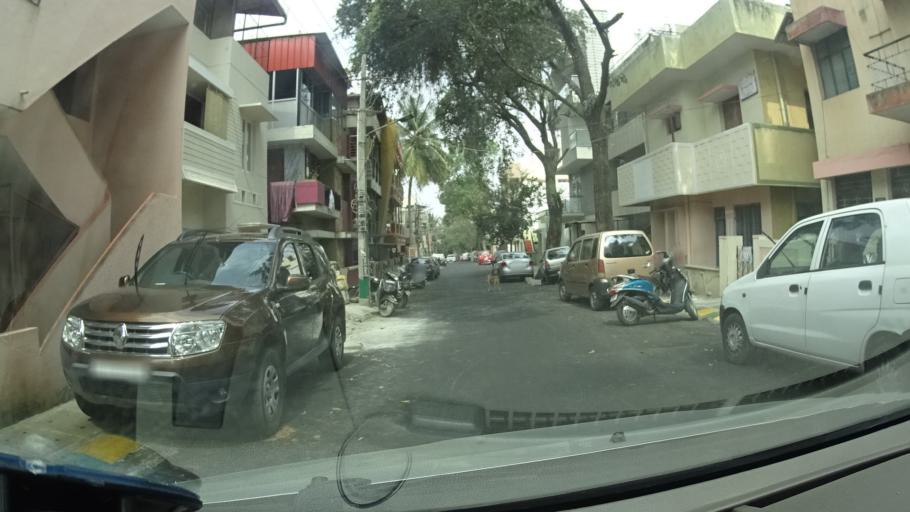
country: IN
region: Karnataka
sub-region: Bangalore Urban
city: Bangalore
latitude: 13.0089
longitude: 77.5499
